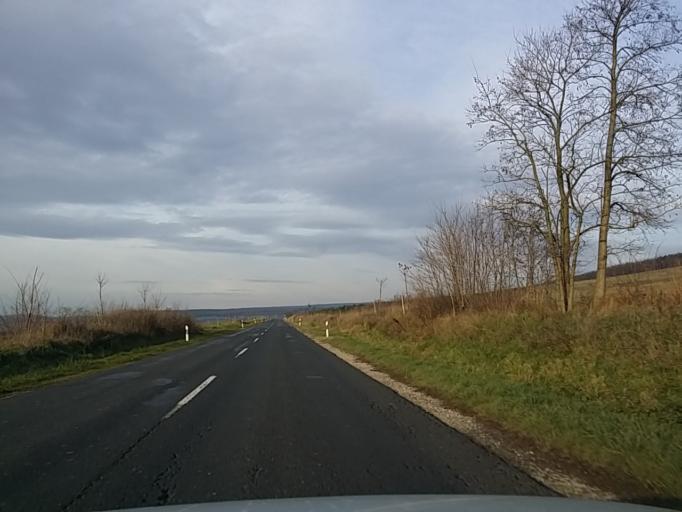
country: HU
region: Veszprem
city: Urkut
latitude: 46.9715
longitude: 17.6273
